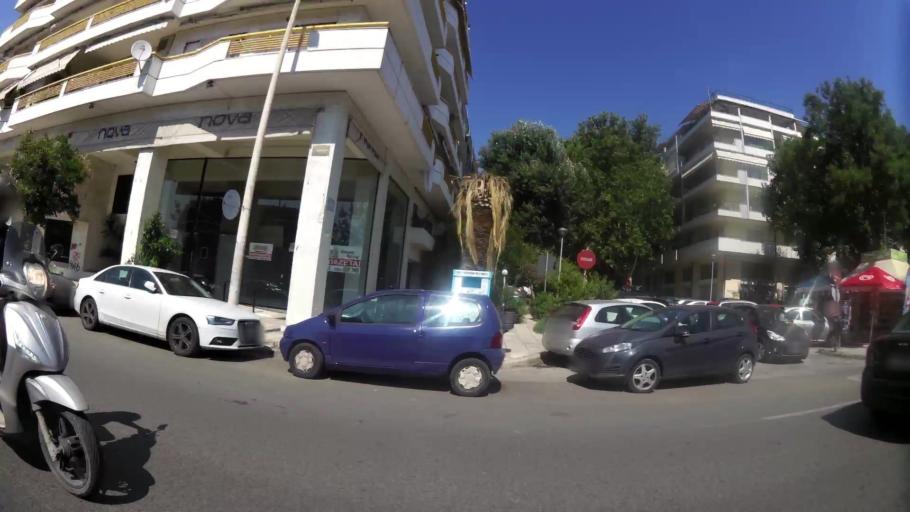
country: GR
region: Central Macedonia
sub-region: Nomos Thessalonikis
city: Kalamaria
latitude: 40.5968
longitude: 22.9529
